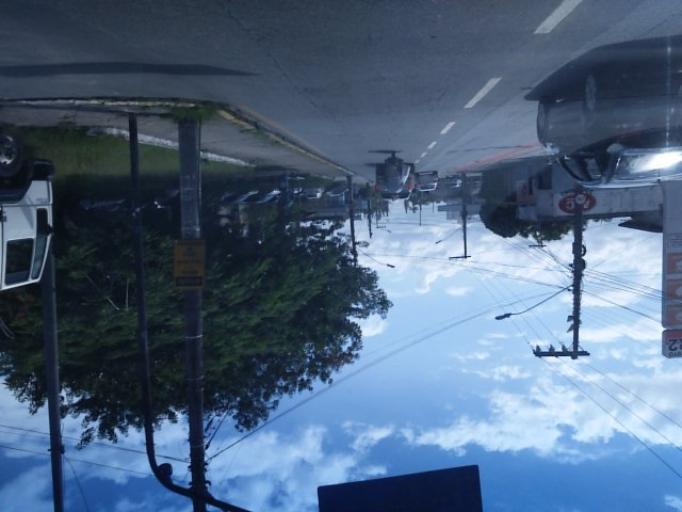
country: BR
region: Santa Catarina
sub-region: Itajai
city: Itajai
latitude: -26.8930
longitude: -48.6752
